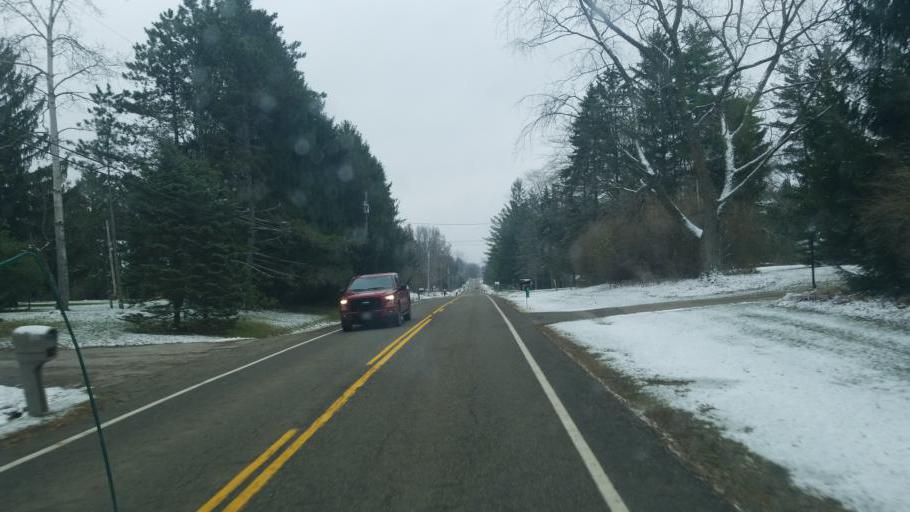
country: US
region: Ohio
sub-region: Cuyahoga County
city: Broadview Heights
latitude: 41.2772
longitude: -81.6699
